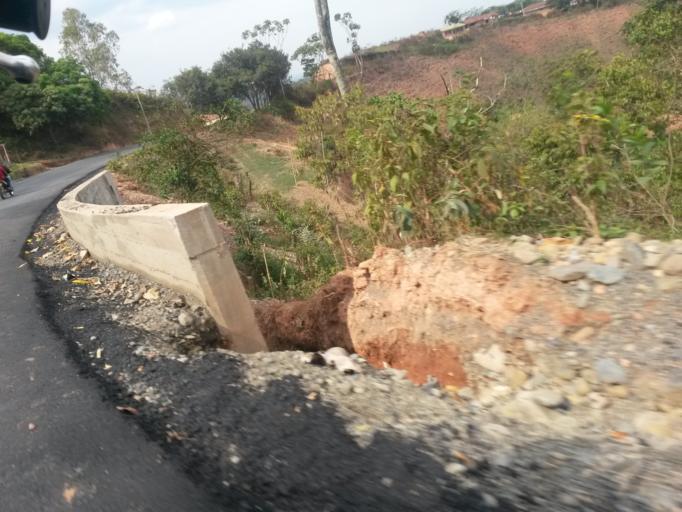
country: CO
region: Cauca
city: Buenos Aires
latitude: 3.0504
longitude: -76.6377
